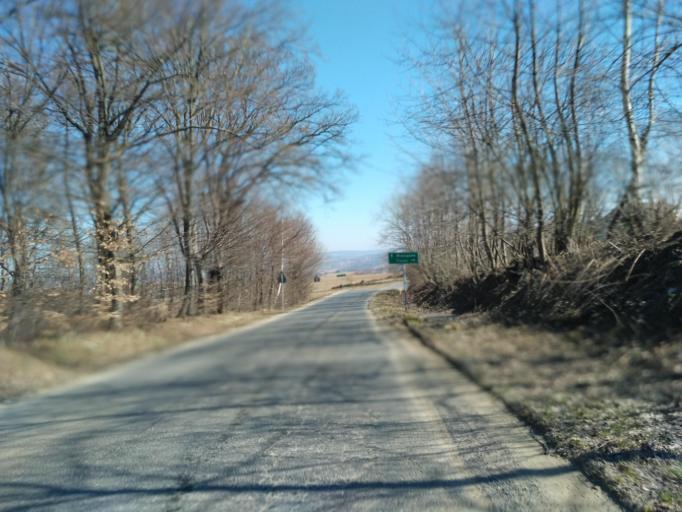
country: PL
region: Subcarpathian Voivodeship
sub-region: Powiat ropczycko-sedziszowski
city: Niedzwiada
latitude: 49.9663
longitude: 21.4665
